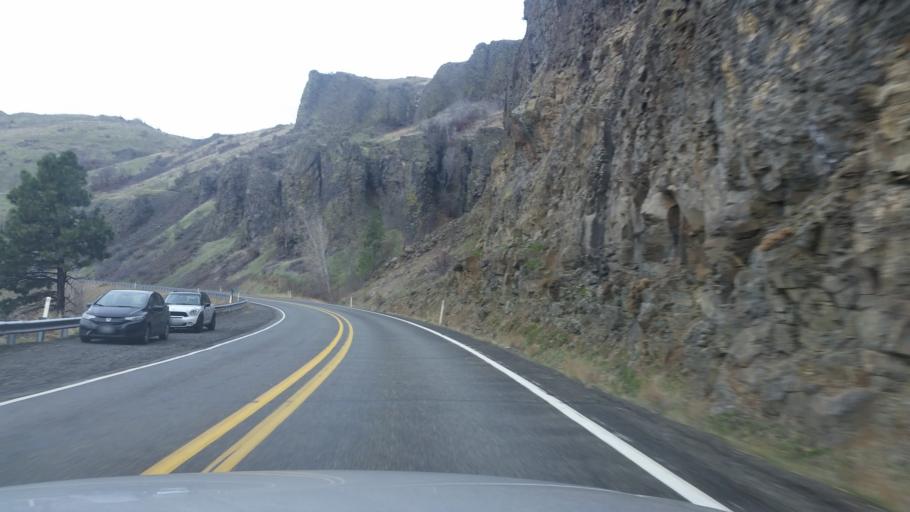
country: US
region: Washington
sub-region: Kittitas County
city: Ellensburg
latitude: 47.1239
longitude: -120.7258
